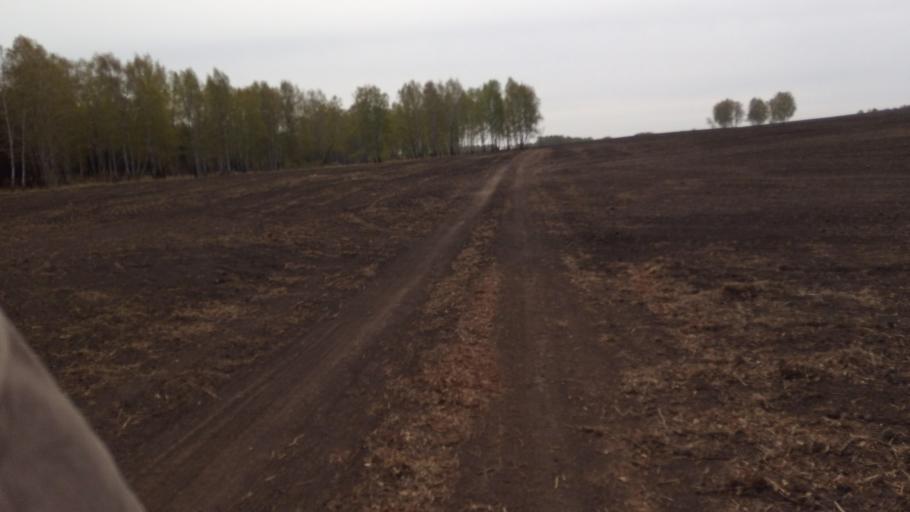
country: RU
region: Chelyabinsk
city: Timiryazevskiy
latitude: 55.0213
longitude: 60.8520
